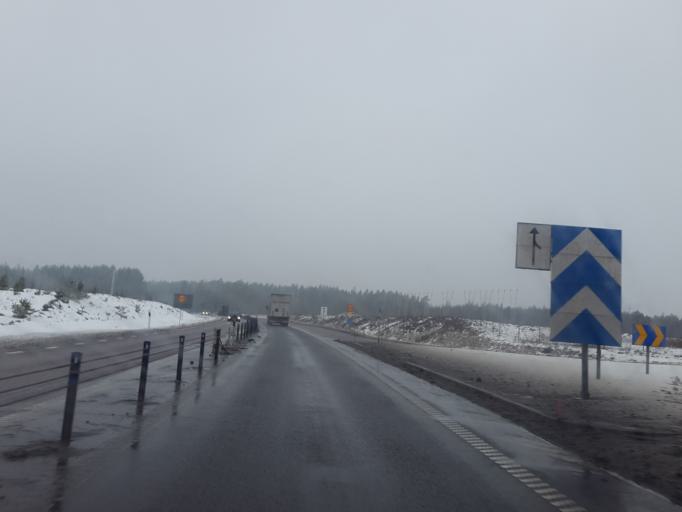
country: SE
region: Joenkoeping
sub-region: Jonkopings Kommun
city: Jonkoping
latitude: 57.7726
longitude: 14.0802
